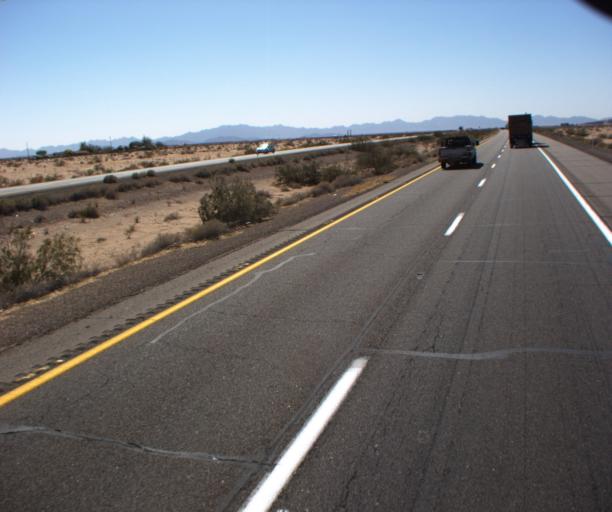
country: US
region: Arizona
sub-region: Yuma County
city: Wellton
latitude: 32.6872
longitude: -113.9953
